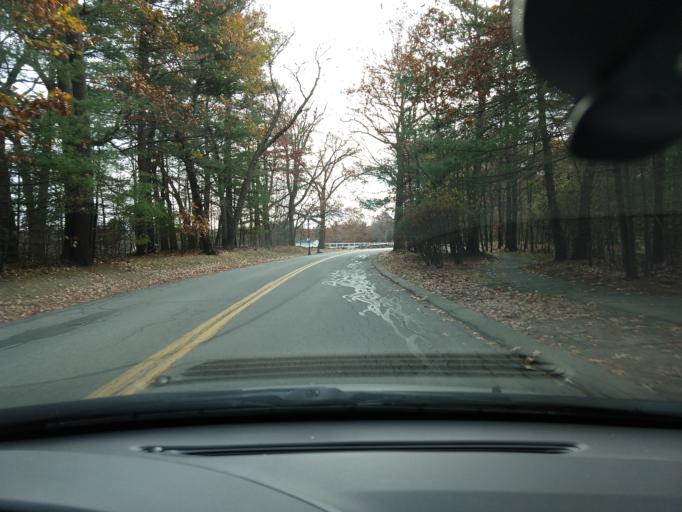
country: US
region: Massachusetts
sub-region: Middlesex County
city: Bedford
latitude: 42.5124
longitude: -71.2929
